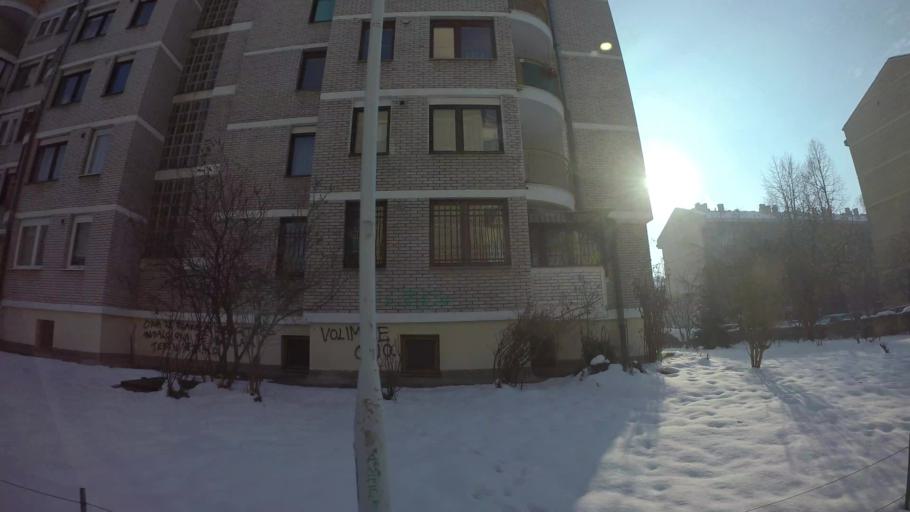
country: BA
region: Federation of Bosnia and Herzegovina
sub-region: Kanton Sarajevo
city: Sarajevo
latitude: 43.8309
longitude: 18.3502
